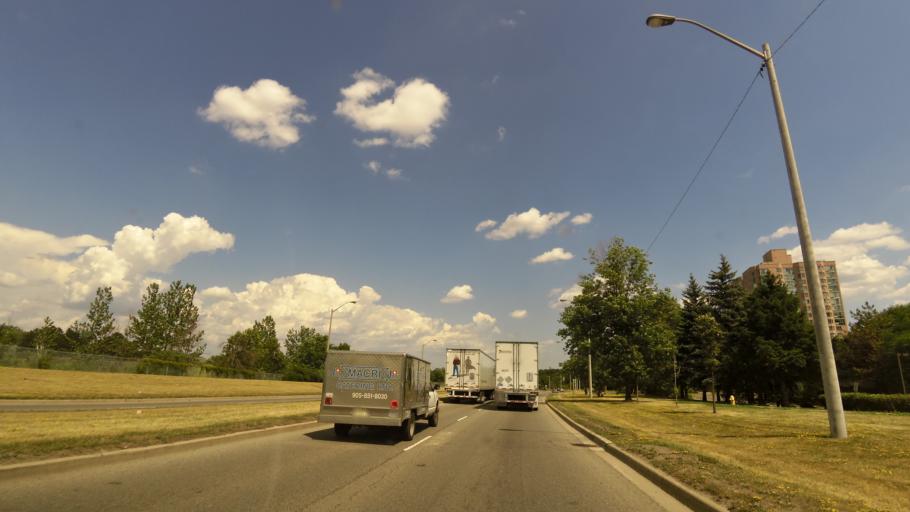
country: CA
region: Ontario
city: Etobicoke
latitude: 43.7598
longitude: -79.5883
